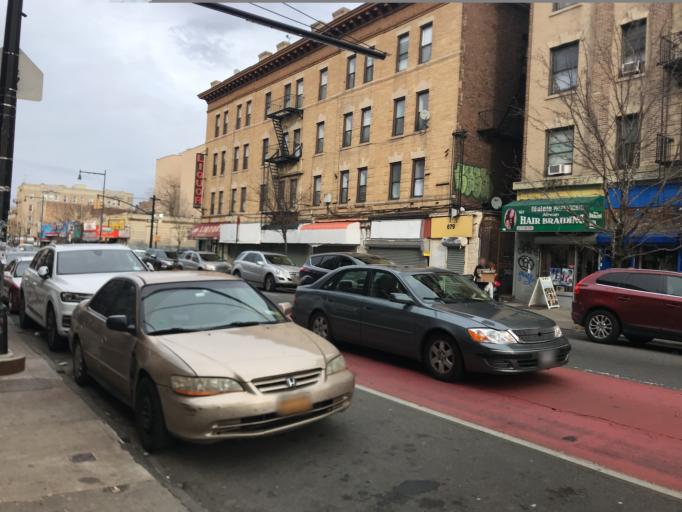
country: US
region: New York
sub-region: Kings County
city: Brooklyn
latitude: 40.6737
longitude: -73.9500
